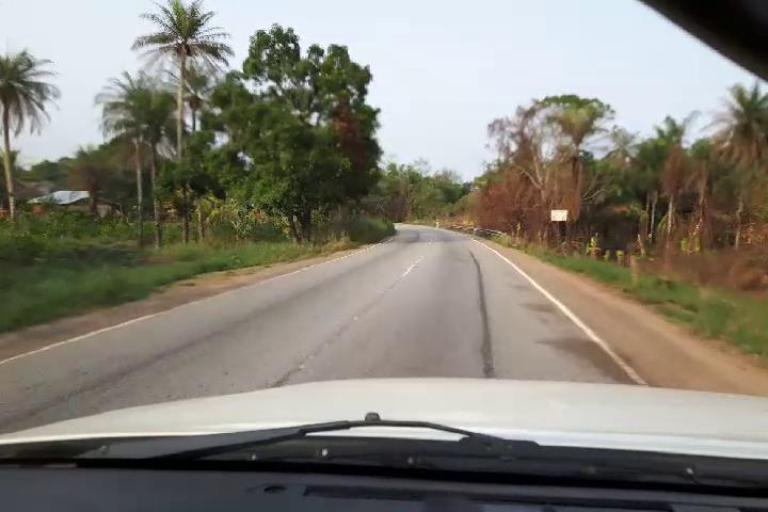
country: SL
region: Southern Province
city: Palima
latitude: 7.9288
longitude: -11.5328
